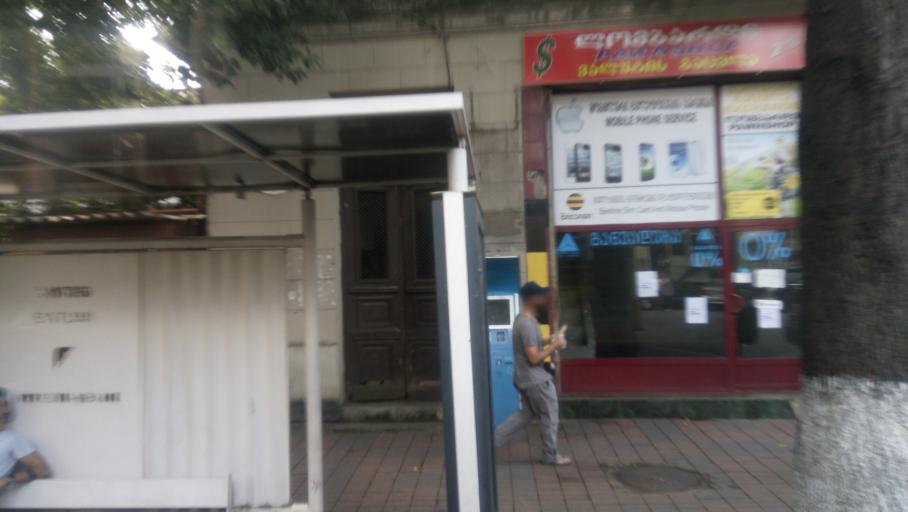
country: GE
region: Ajaria
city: Batumi
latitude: 41.6483
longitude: 41.6379
